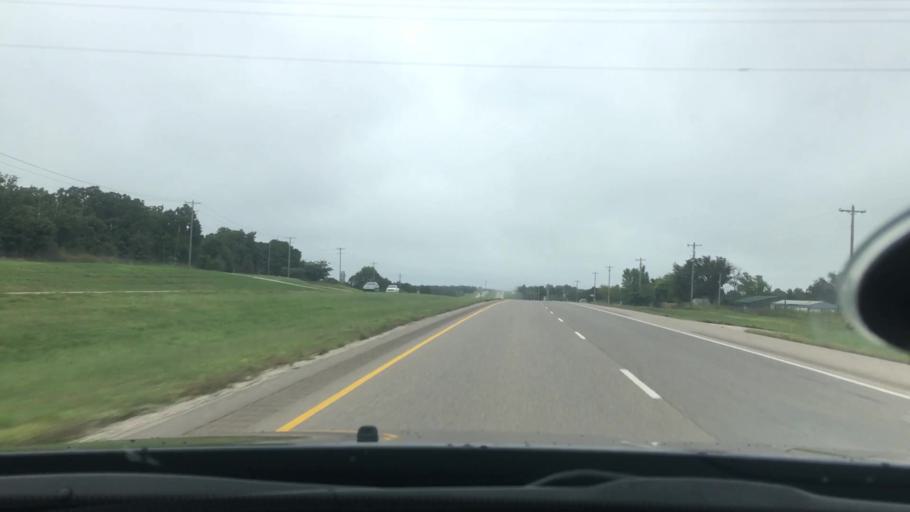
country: US
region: Oklahoma
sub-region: Seminole County
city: Seminole
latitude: 35.3311
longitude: -96.6714
